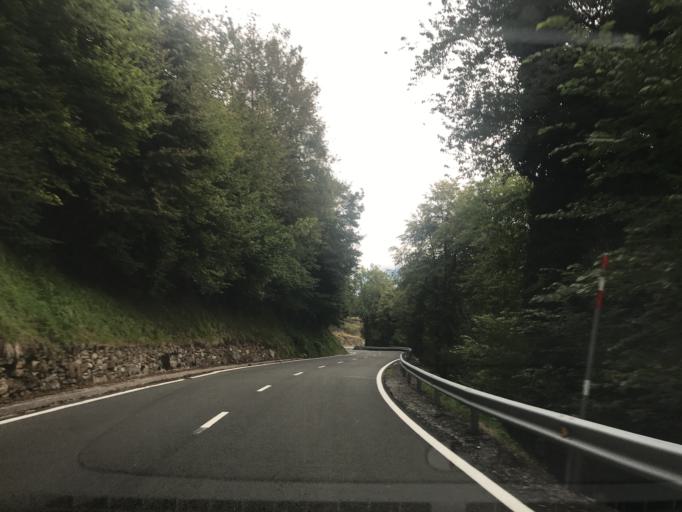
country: ES
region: Catalonia
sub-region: Provincia de Lleida
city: Les
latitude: 42.7765
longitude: 0.6779
